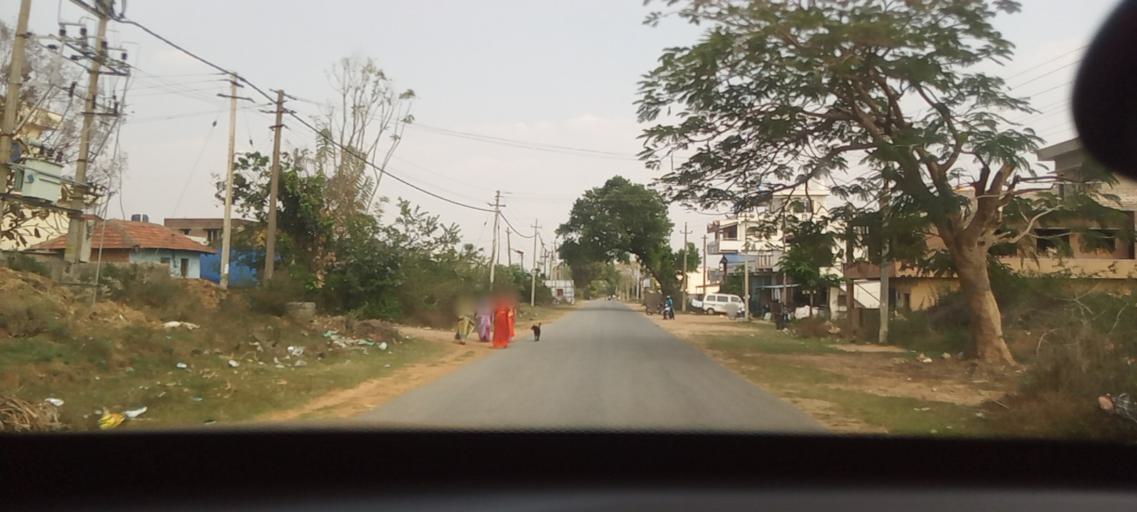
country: IN
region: Karnataka
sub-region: Hassan
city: Belur
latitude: 13.1742
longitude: 75.8544
